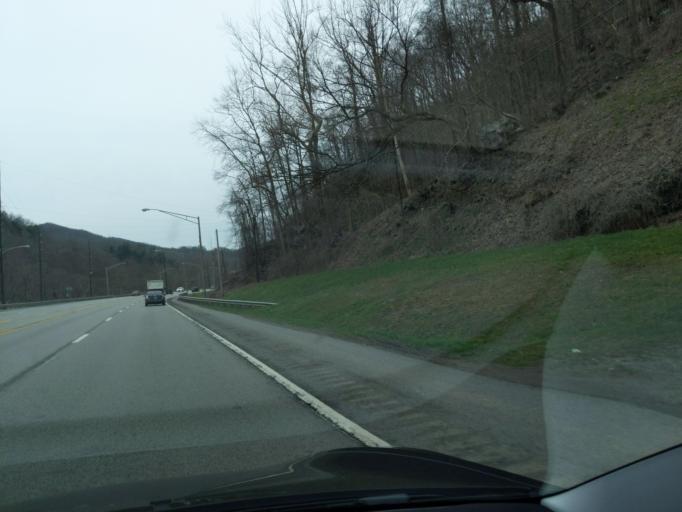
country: US
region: Kentucky
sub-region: Bell County
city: Pineville
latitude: 36.7541
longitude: -83.6932
